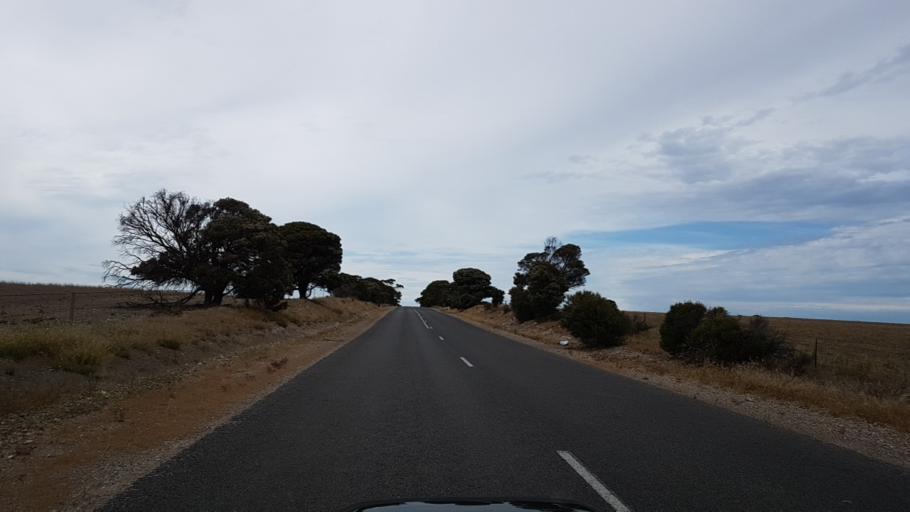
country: AU
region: South Australia
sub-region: Yorke Peninsula
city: Honiton
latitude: -34.9474
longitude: 137.0970
